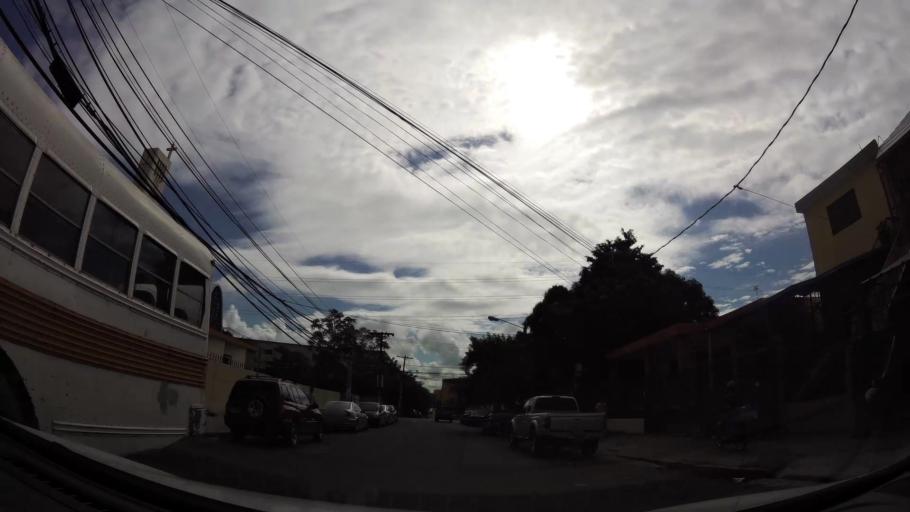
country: DO
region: Santo Domingo
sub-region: Santo Domingo
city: Santo Domingo Este
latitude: 18.4861
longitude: -69.8662
